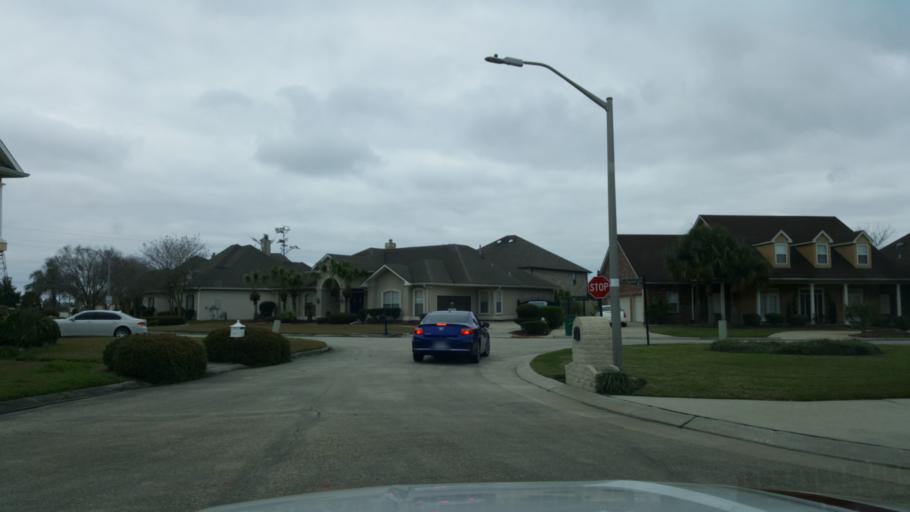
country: US
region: Louisiana
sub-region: Jefferson Parish
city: Woodmere
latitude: 29.8778
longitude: -90.0812
